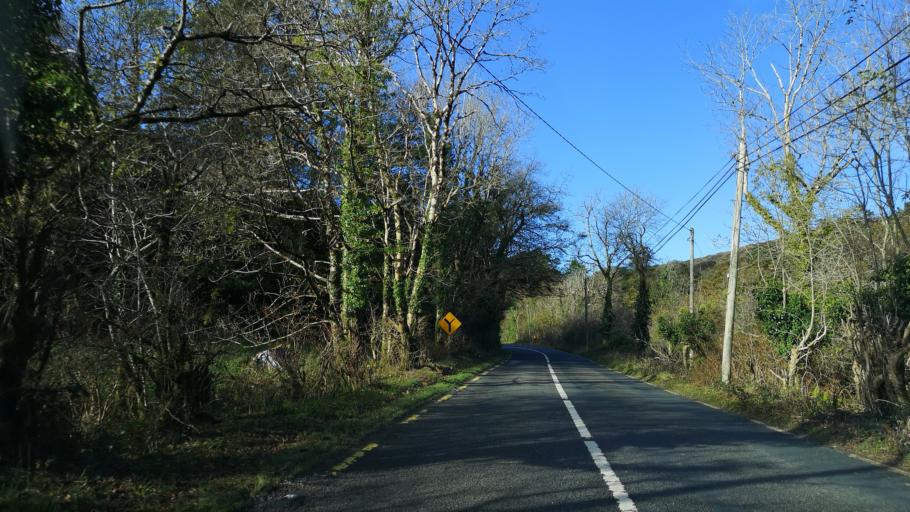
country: IE
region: Connaught
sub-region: County Galway
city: Clifden
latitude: 53.5607
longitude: -9.9150
